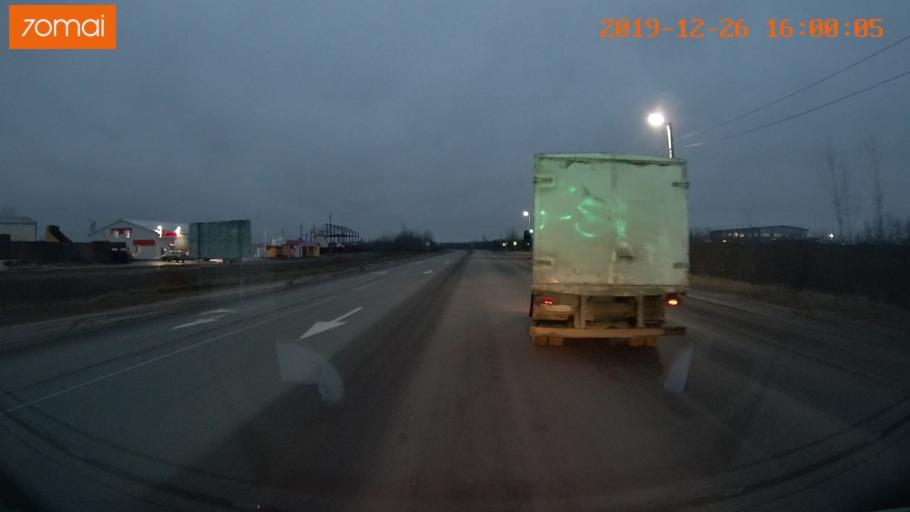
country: RU
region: Jaroslavl
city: Rybinsk
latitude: 58.0278
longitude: 38.8036
